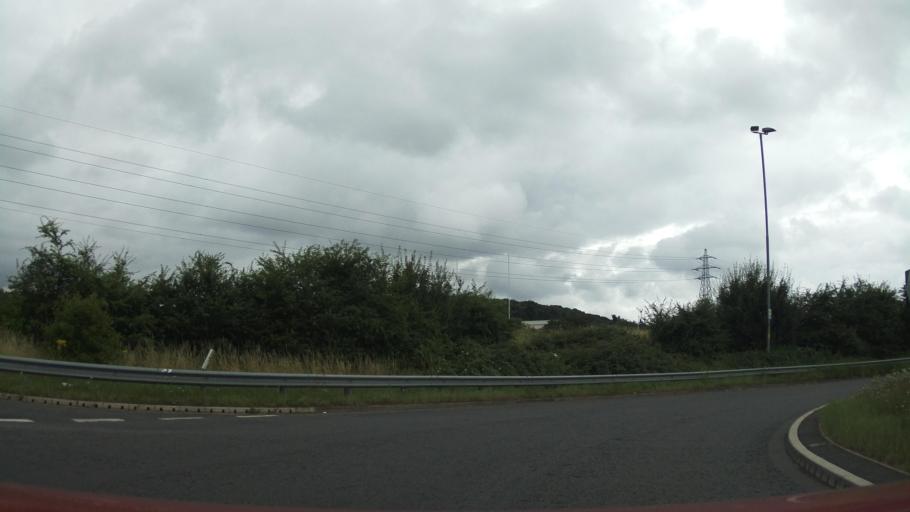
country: GB
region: England
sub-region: Worcestershire
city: Fernhill Heath
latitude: 52.2173
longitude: -2.1605
